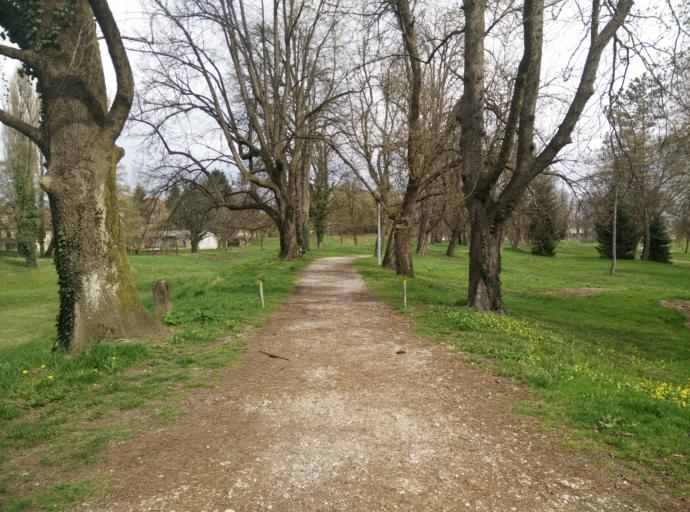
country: HR
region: Karlovacka
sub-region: Grad Karlovac
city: Karlovac
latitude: 45.4915
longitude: 15.5588
